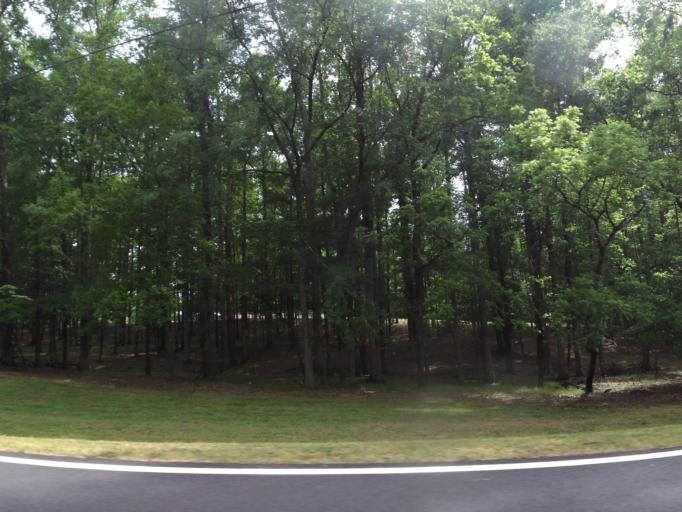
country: US
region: Georgia
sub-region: McDuffie County
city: Thomson
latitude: 33.5303
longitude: -82.4829
